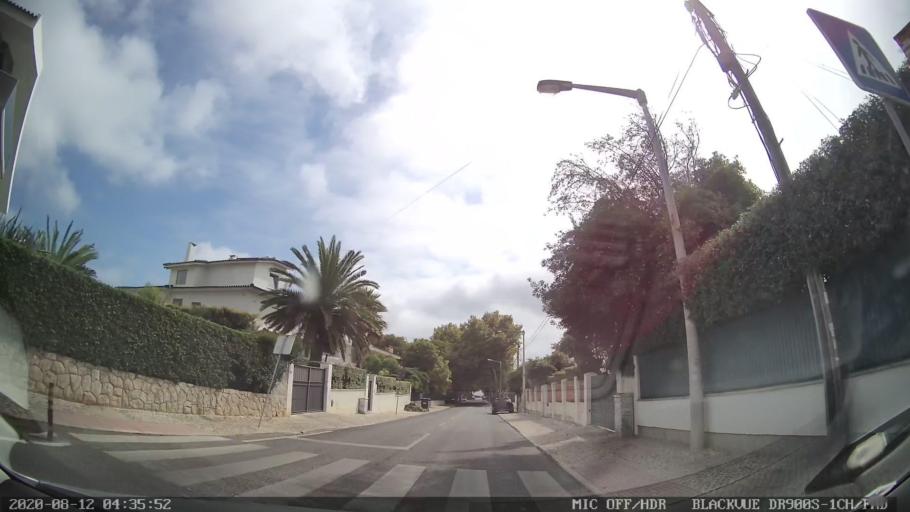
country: PT
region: Lisbon
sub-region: Cascais
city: Estoril
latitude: 38.6993
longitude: -9.3779
